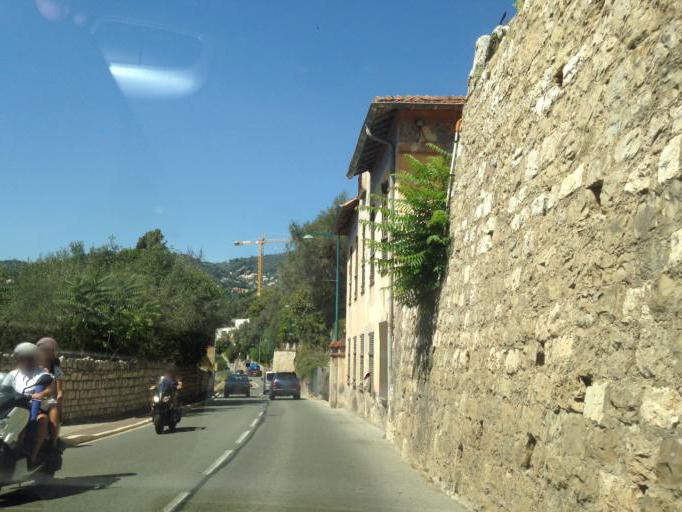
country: FR
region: Provence-Alpes-Cote d'Azur
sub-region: Departement des Alpes-Maritimes
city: Saint-Jean-Cap-Ferrat
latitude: 43.6952
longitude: 7.3281
